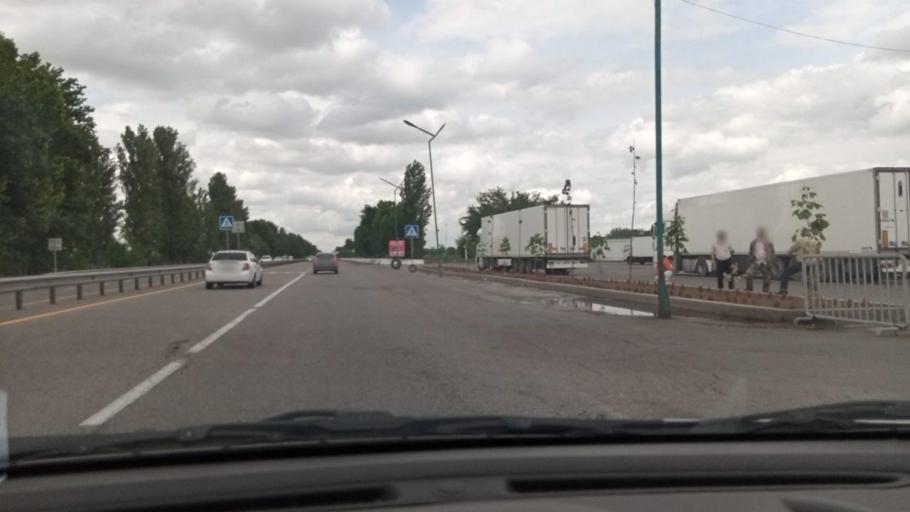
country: UZ
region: Toshkent Shahri
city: Bektemir
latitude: 41.2084
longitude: 69.4029
